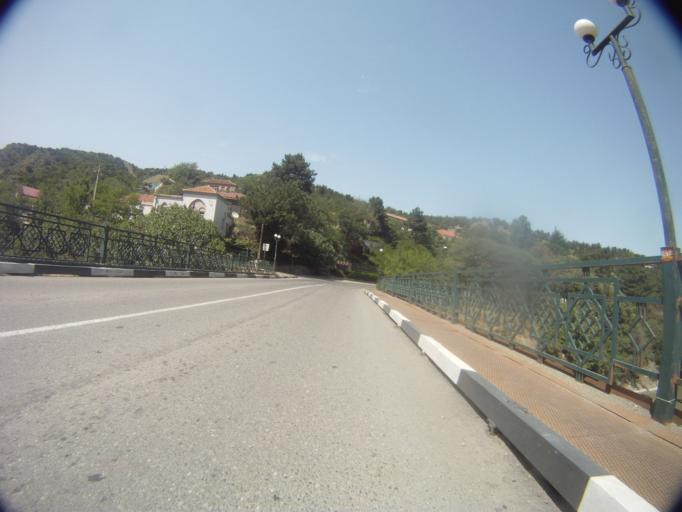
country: GE
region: Mtskheta-Mtianeti
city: Mtskheta
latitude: 41.8379
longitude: 44.7052
